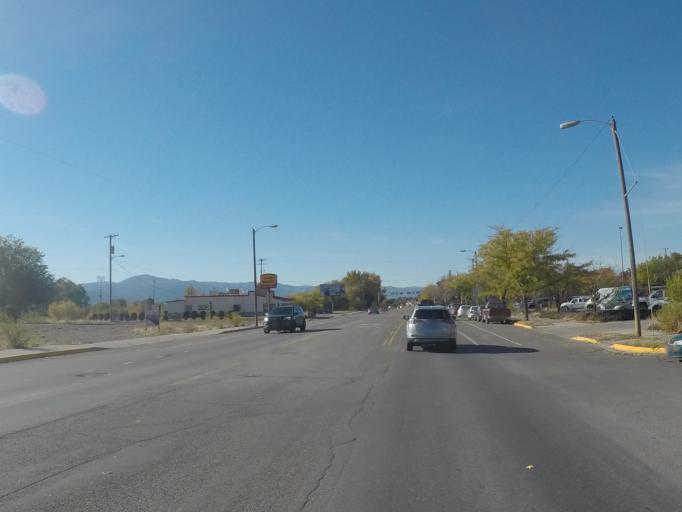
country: US
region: Montana
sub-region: Missoula County
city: Missoula
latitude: 46.8744
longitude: -114.0017
